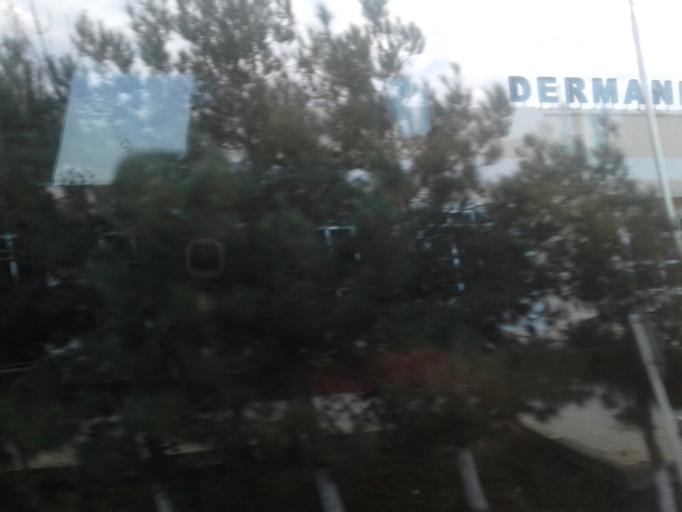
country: TM
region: Mary
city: Seydi
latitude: 39.2601
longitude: 63.1891
